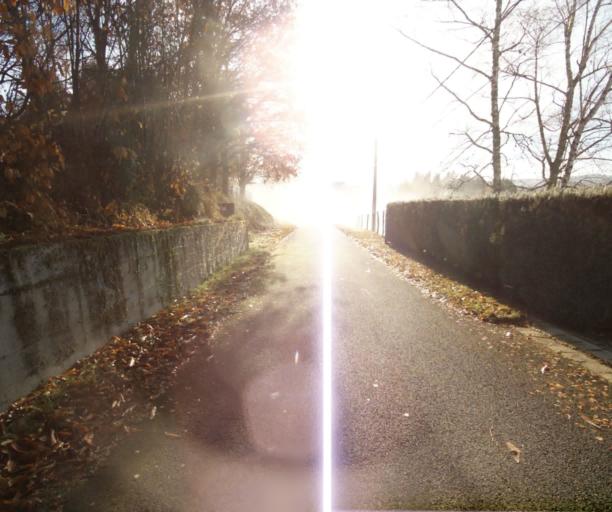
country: FR
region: Limousin
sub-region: Departement de la Correze
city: Laguenne
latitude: 45.2545
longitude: 1.7956
